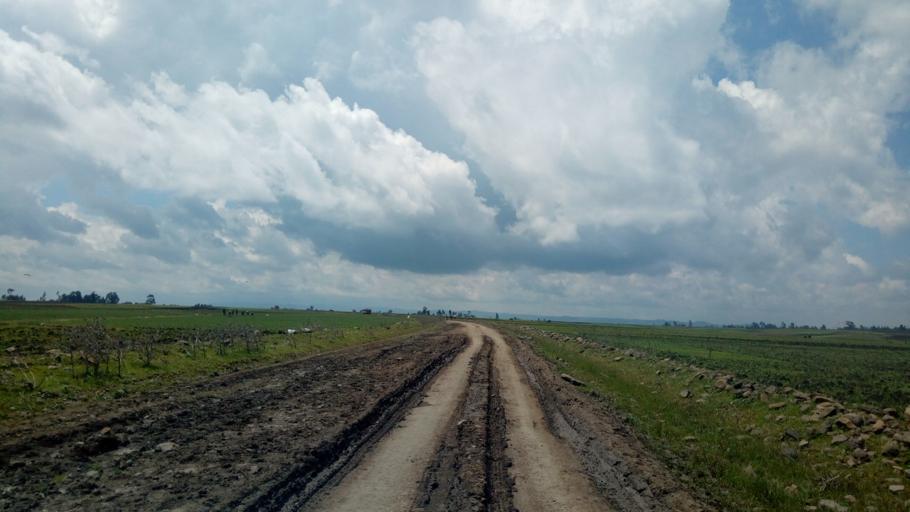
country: ET
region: Oromiya
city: Sendafa
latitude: 9.0043
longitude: 39.1255
